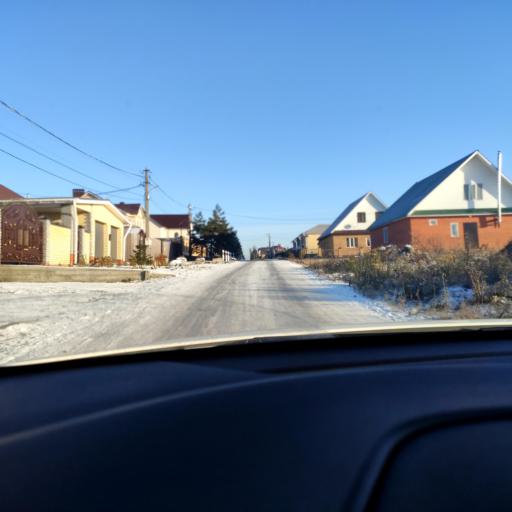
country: RU
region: Tatarstan
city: Vysokaya Gora
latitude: 55.8125
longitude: 49.2493
